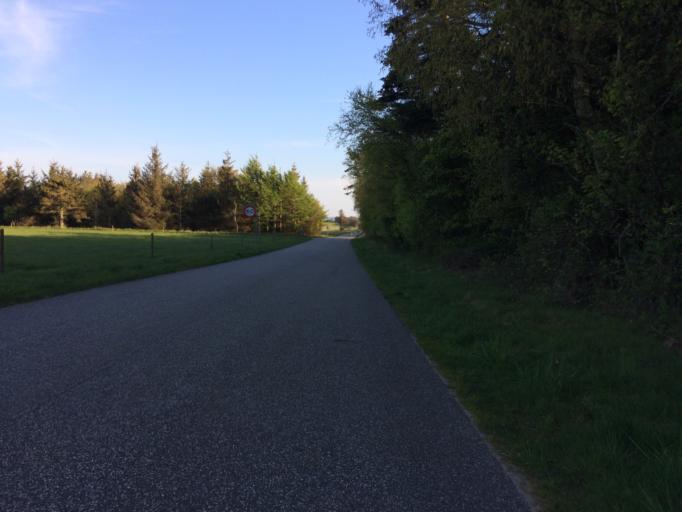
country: DK
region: Central Jutland
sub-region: Struer Kommune
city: Struer
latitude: 56.5439
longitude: 8.6251
